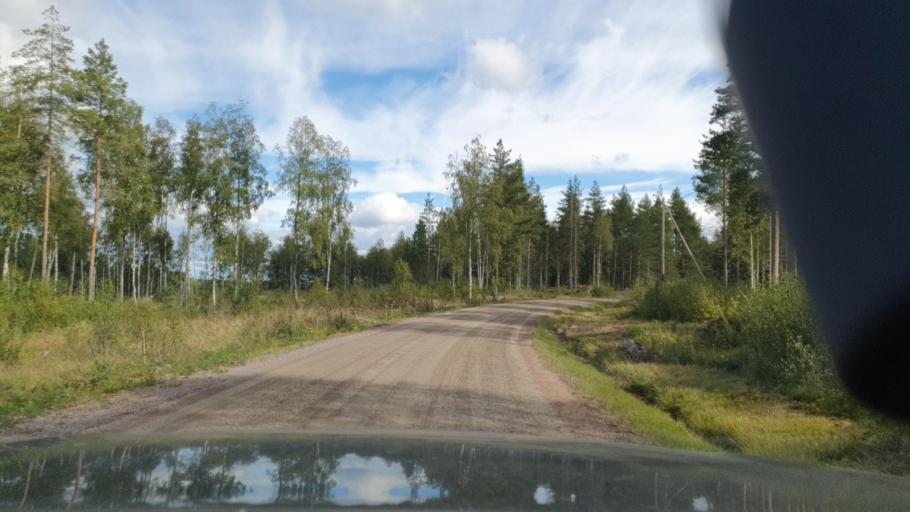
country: SE
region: Vaermland
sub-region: Filipstads Kommun
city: Filipstad
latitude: 59.5495
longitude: 14.0789
